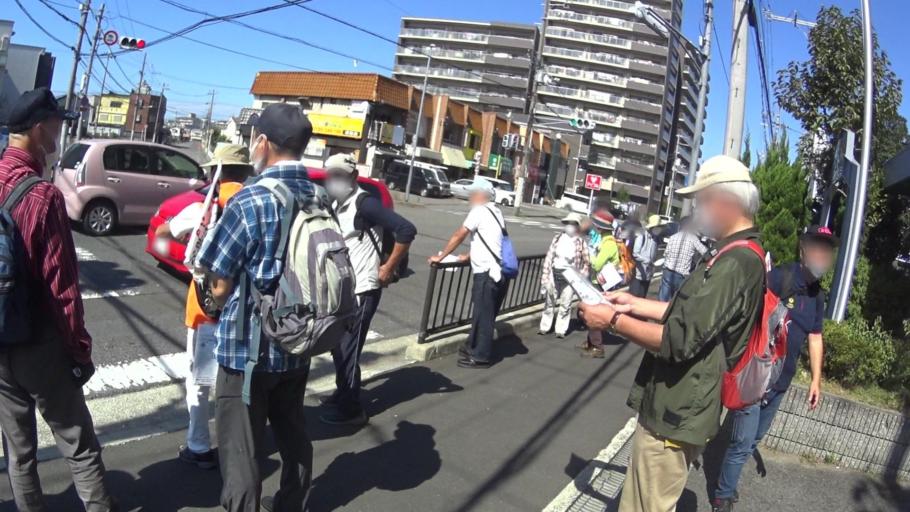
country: JP
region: Osaka
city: Takaishi
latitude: 34.5213
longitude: 135.4827
